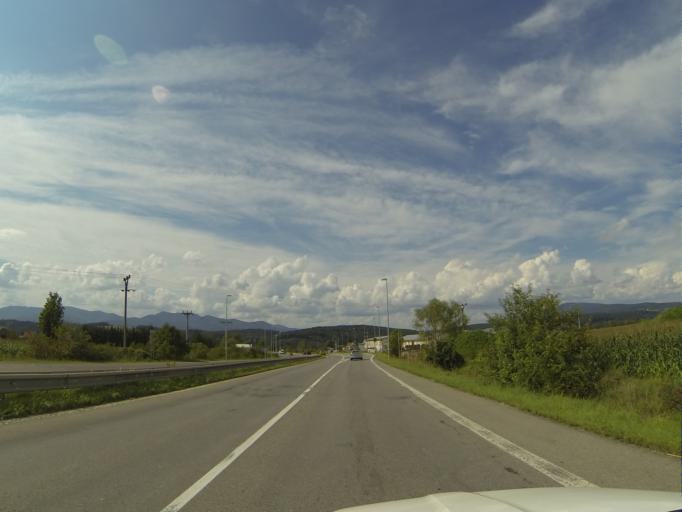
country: SK
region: Nitriansky
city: Novaky
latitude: 48.7226
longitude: 18.5564
